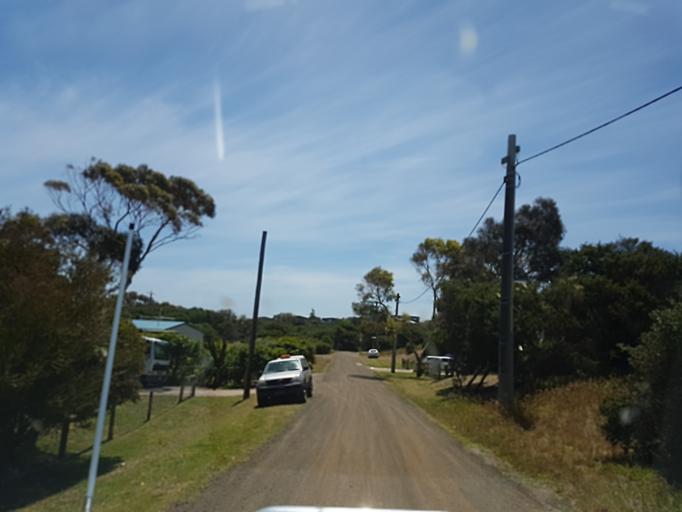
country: AU
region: Victoria
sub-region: Bass Coast
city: North Wonthaggi
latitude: -38.7012
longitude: 145.8269
